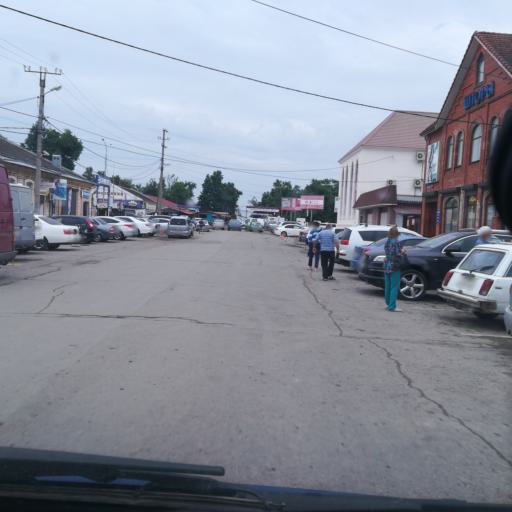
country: RU
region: Krasnodarskiy
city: Slavyansk-na-Kubani
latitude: 45.2630
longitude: 38.1300
